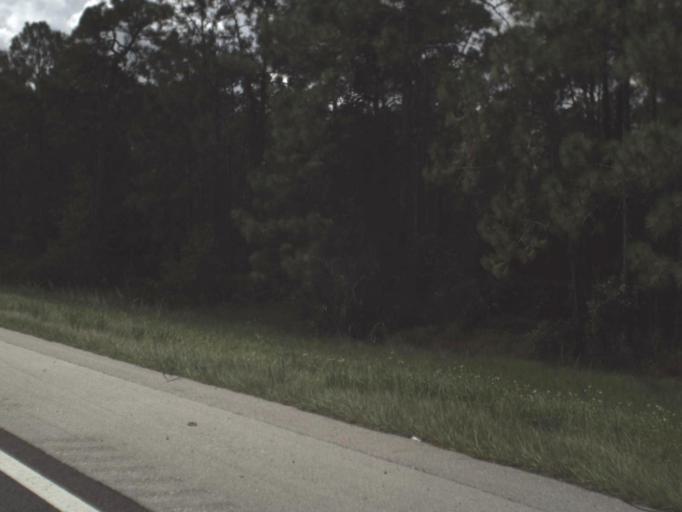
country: US
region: Florida
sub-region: Collier County
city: Vineyards
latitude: 26.2591
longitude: -81.7423
